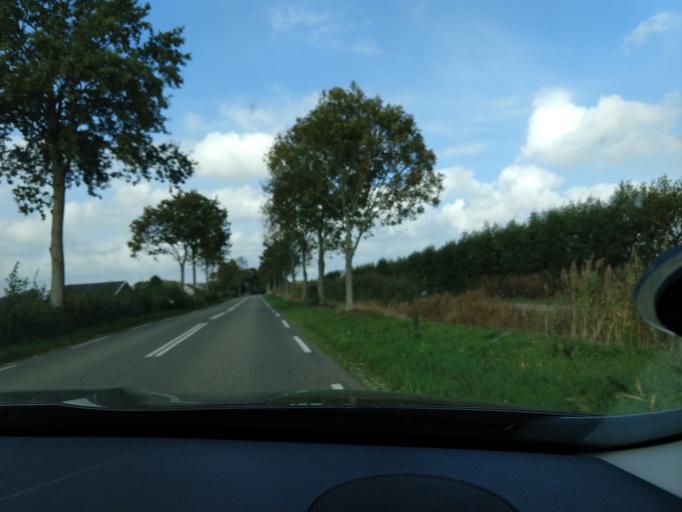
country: NL
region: Zeeland
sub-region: Schouwen-Duiveland
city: Bruinisse
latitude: 51.6660
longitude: 4.0424
